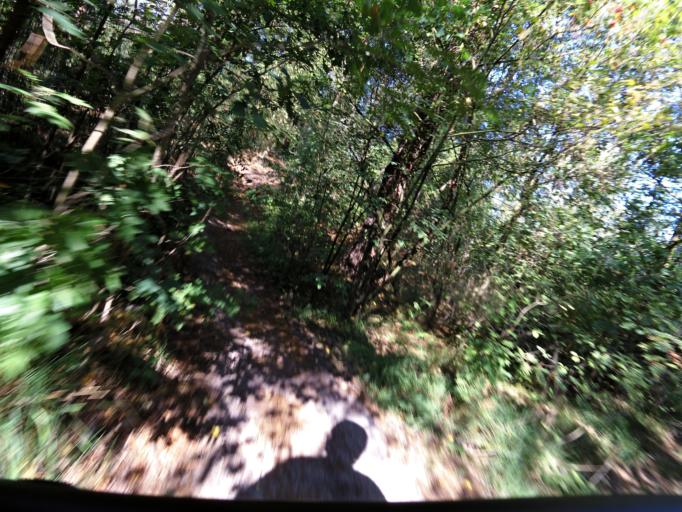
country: BE
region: Flanders
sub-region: Provincie Antwerpen
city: Stabroek
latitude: 51.3638
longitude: 4.3416
